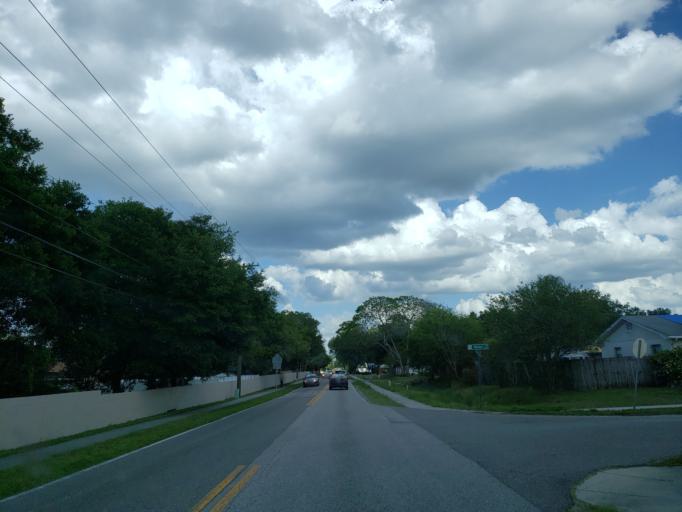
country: US
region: Florida
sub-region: Hillsborough County
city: Mango
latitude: 27.9597
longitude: -82.3010
